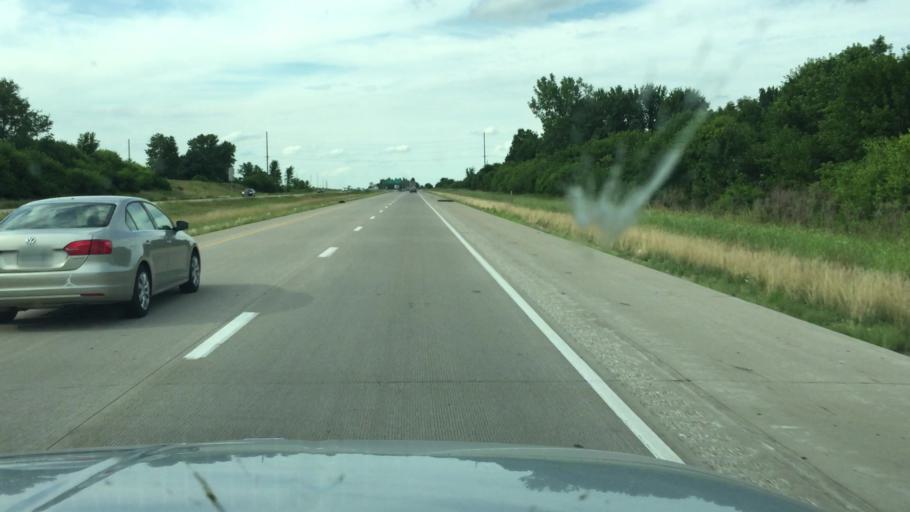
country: US
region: Iowa
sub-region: Scott County
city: Walcott
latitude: 41.5786
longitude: -90.6768
